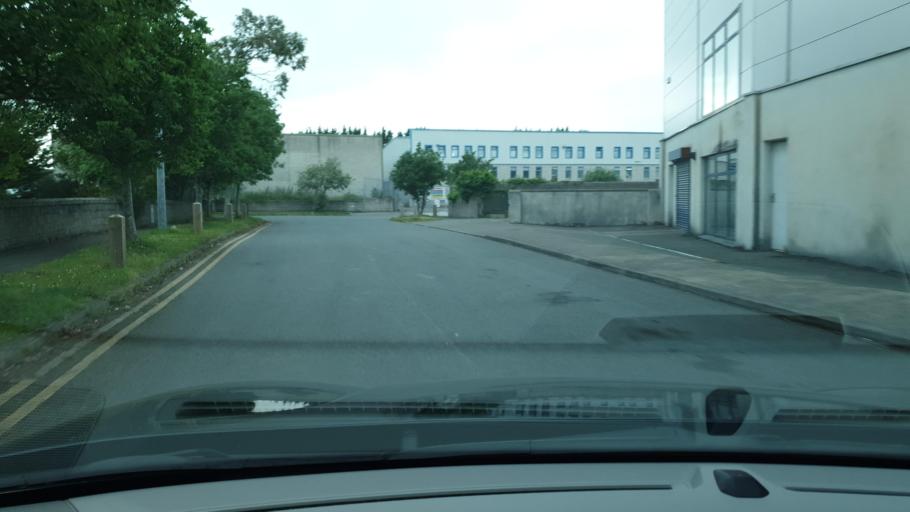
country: IE
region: Leinster
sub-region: An Mhi
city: Ashbourne
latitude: 53.5185
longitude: -6.4096
